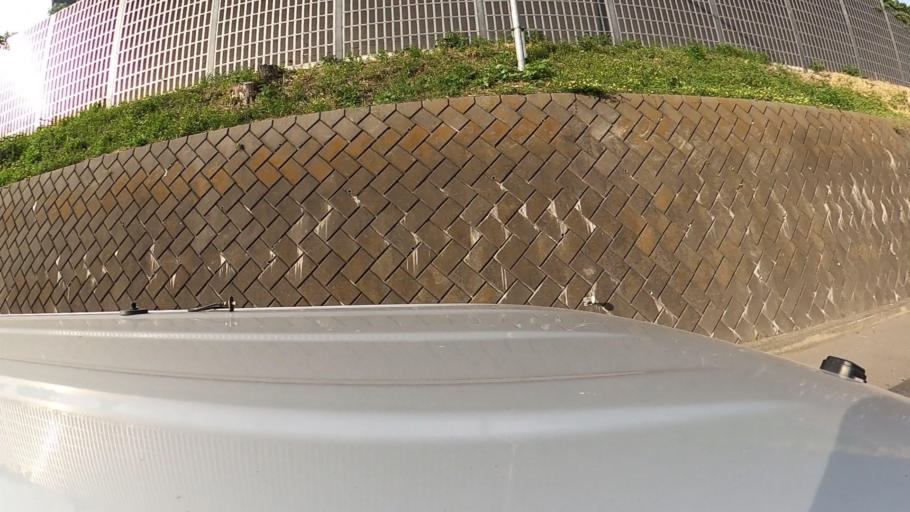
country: JP
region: Saitama
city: Asaka
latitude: 35.7873
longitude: 139.5529
